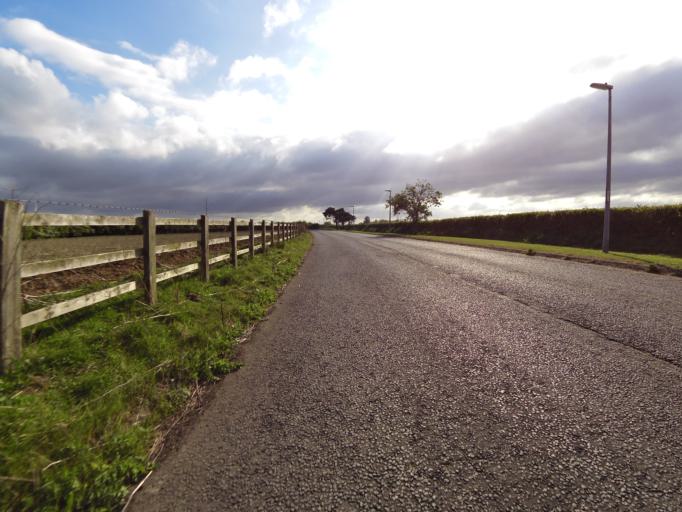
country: GB
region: England
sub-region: Cambridgeshire
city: Fulbourn
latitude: 52.2155
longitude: 0.2153
